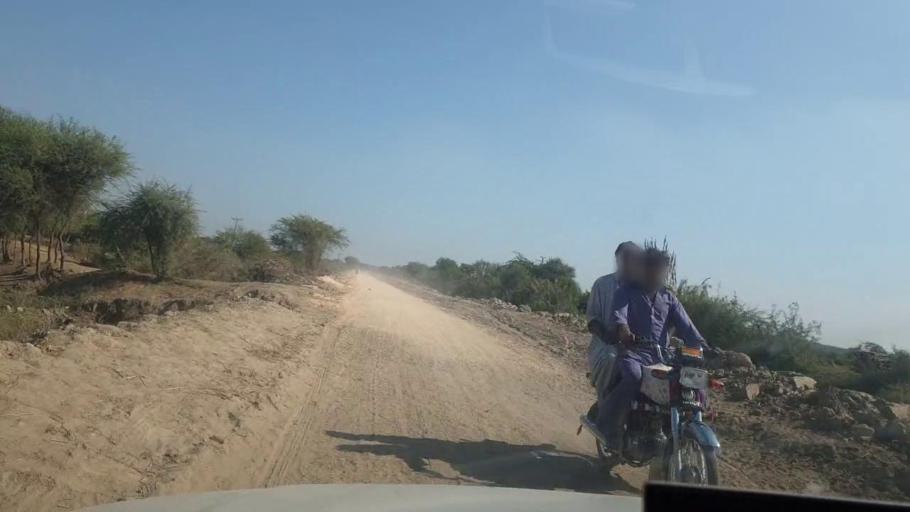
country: PK
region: Sindh
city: Kotri
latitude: 25.1624
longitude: 68.3002
